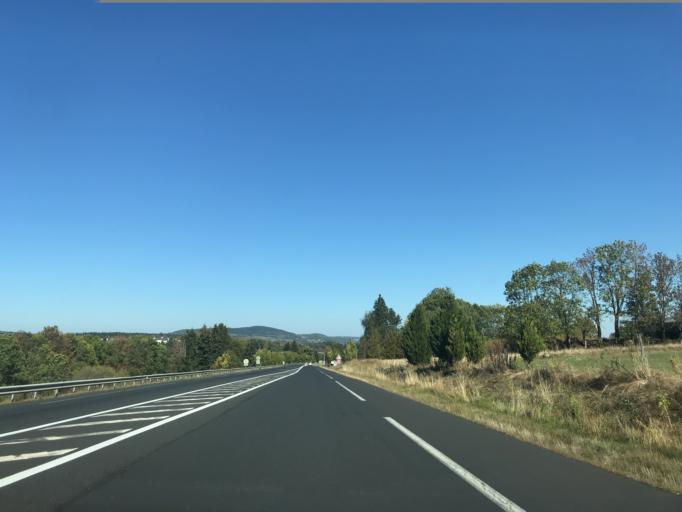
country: FR
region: Auvergne
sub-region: Departement du Puy-de-Dome
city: Gelles
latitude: 45.6808
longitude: 2.7975
